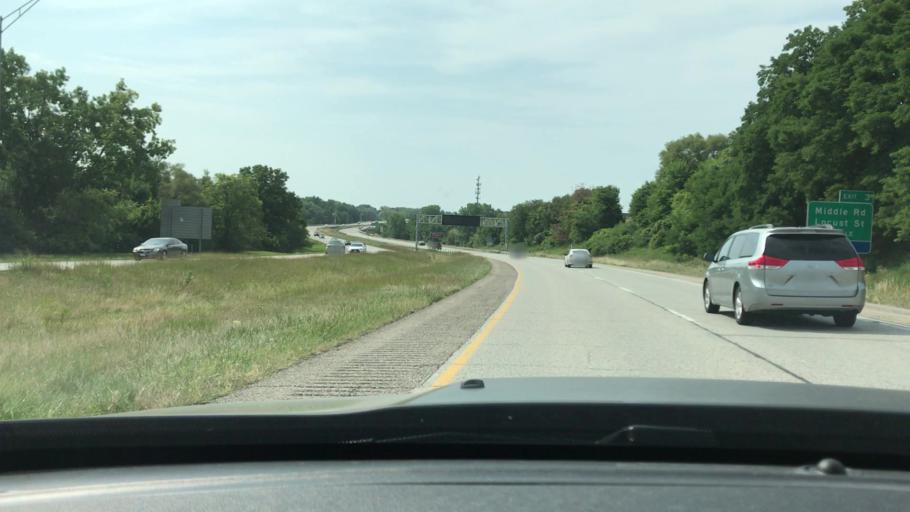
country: US
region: Iowa
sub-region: Scott County
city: Bettendorf
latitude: 41.5502
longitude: -90.5217
